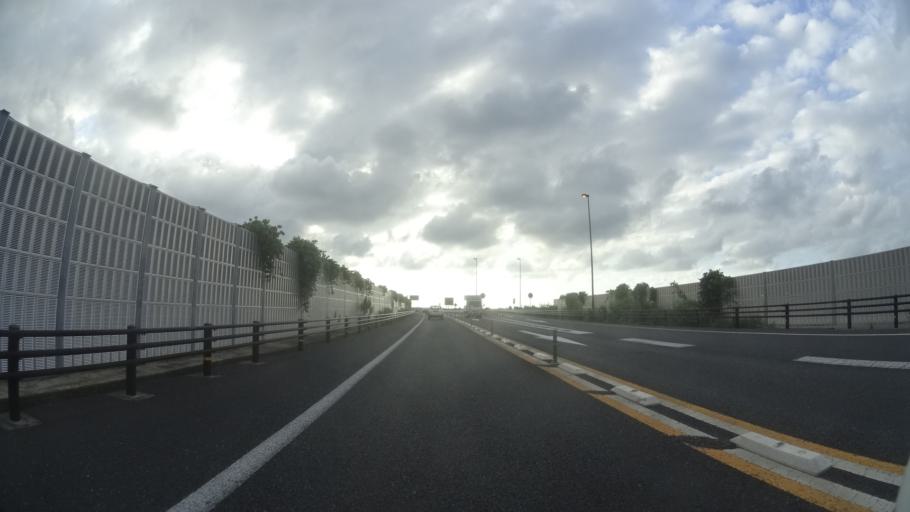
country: JP
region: Tottori
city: Kurayoshi
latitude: 35.5090
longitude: 133.6375
